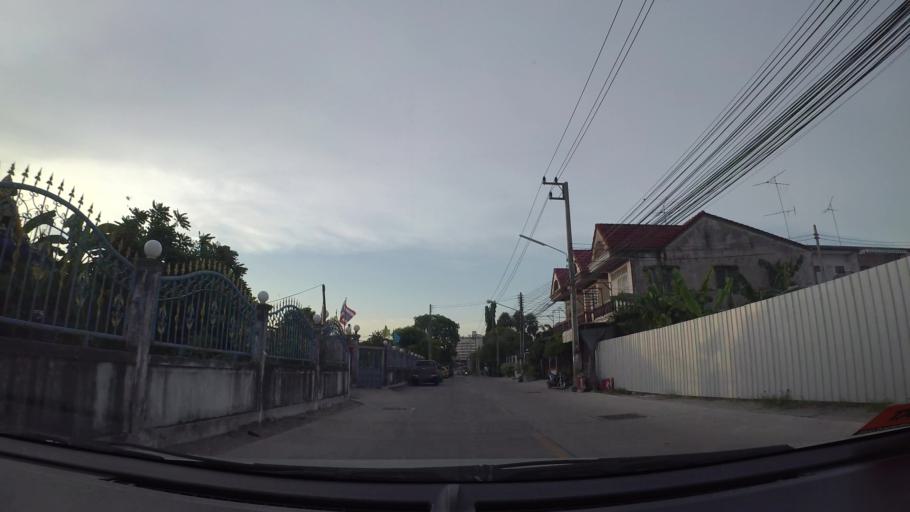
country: TH
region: Chon Buri
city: Chon Buri
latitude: 13.3450
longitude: 100.9827
